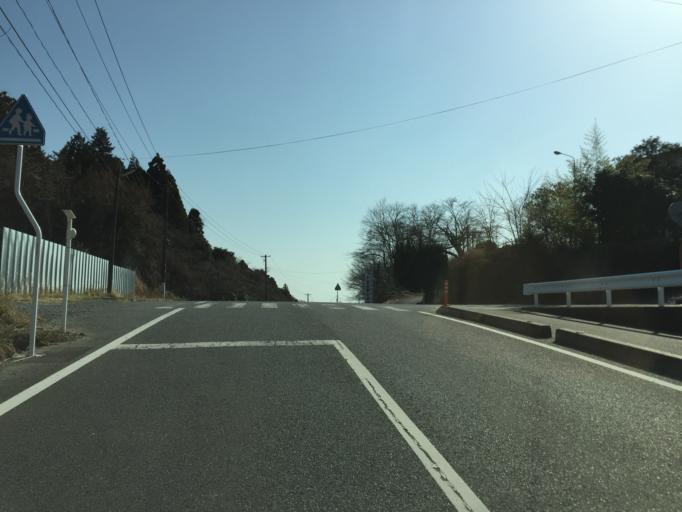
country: JP
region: Fukushima
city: Iwaki
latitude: 36.9667
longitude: 140.8987
